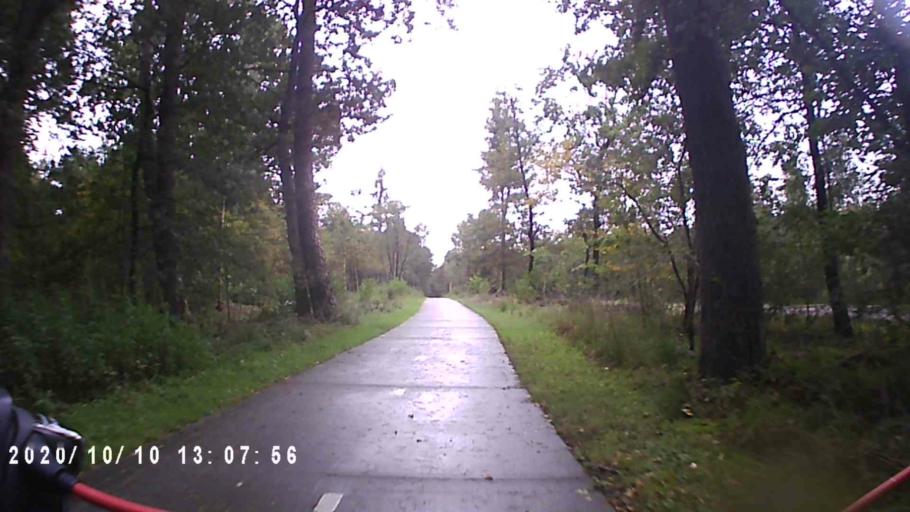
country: NL
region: Drenthe
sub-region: Gemeente Westerveld
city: Dwingeloo
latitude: 52.8751
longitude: 6.3222
